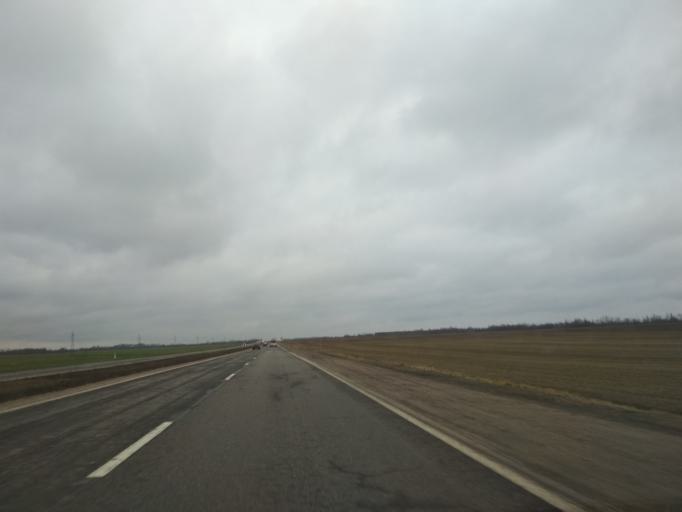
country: BY
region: Minsk
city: Dukora
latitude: 53.6557
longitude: 27.9591
